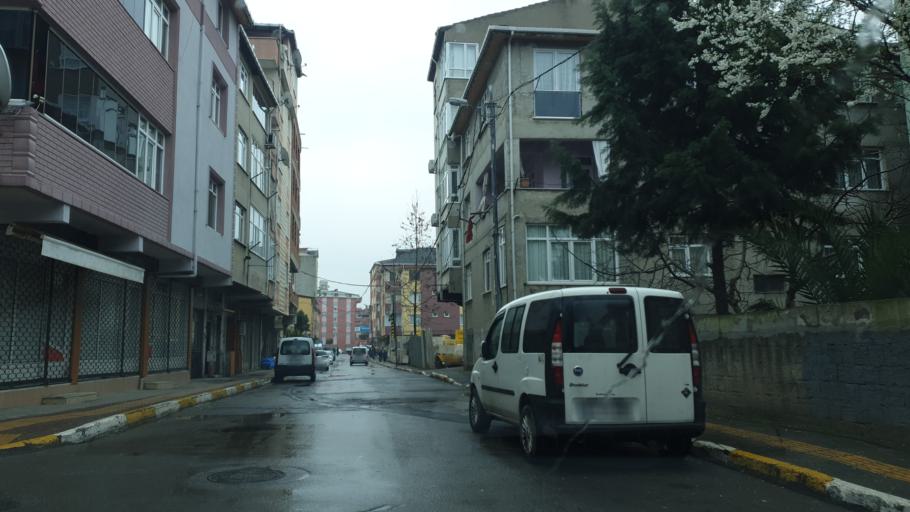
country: TR
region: Istanbul
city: Pendik
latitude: 40.8850
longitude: 29.2709
